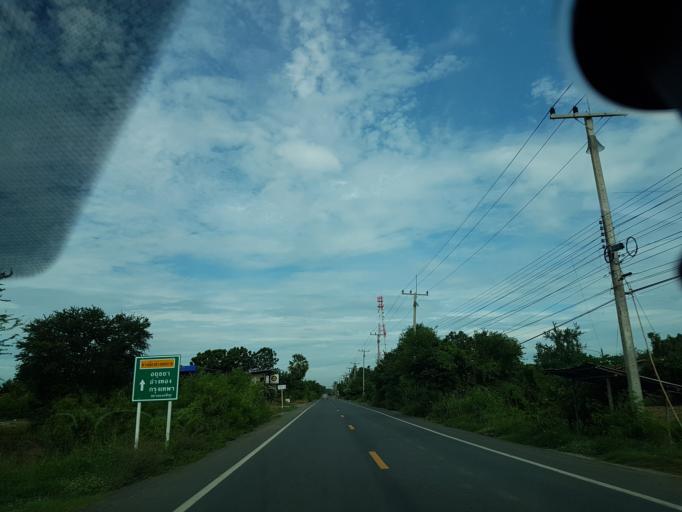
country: TH
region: Lop Buri
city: Tha Wung
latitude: 14.7411
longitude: 100.5365
